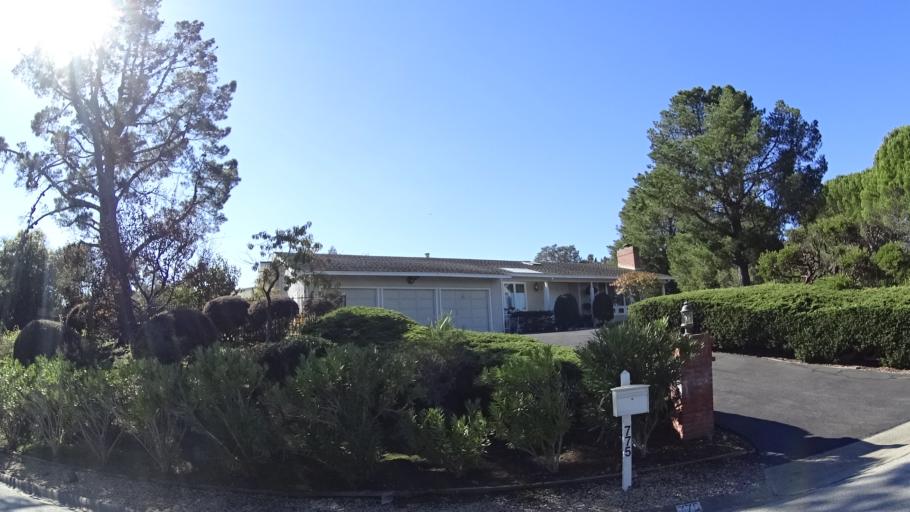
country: US
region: California
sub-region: San Mateo County
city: Hillsborough
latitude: 37.5579
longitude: -122.3784
